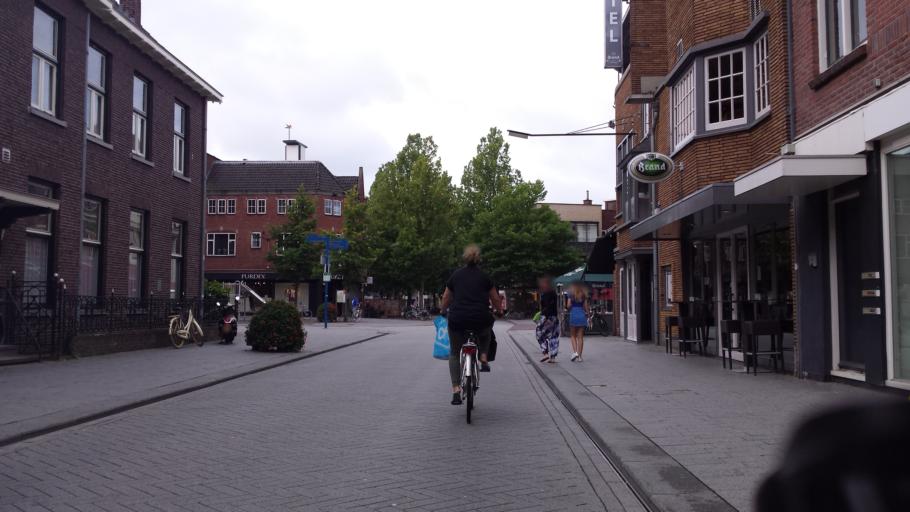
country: NL
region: Overijssel
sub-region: Gemeente Hengelo
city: Hengelo
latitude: 52.2657
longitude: 6.7935
